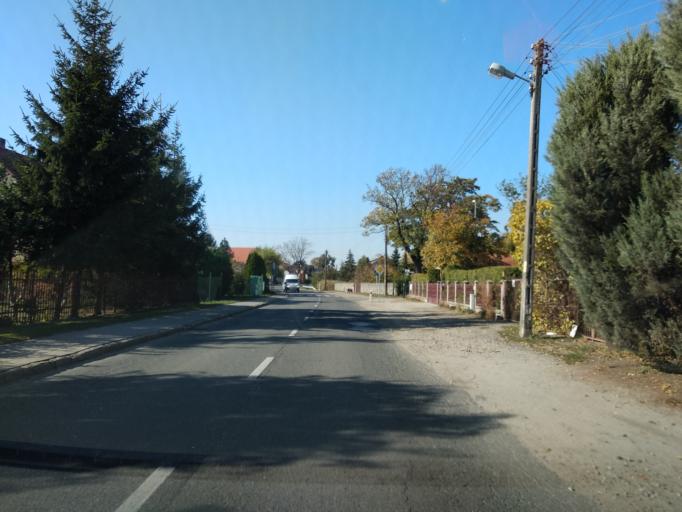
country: PL
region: Lower Silesian Voivodeship
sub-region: Powiat wroclawski
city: Bielany Wroclawskie
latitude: 51.0709
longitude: 16.9354
